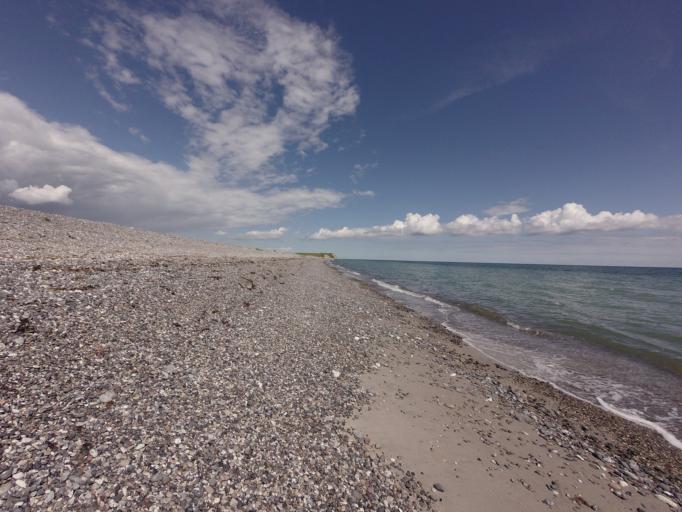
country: DK
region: Central Jutland
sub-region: Norddjurs Kommune
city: Grenaa
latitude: 56.4965
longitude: 10.8702
